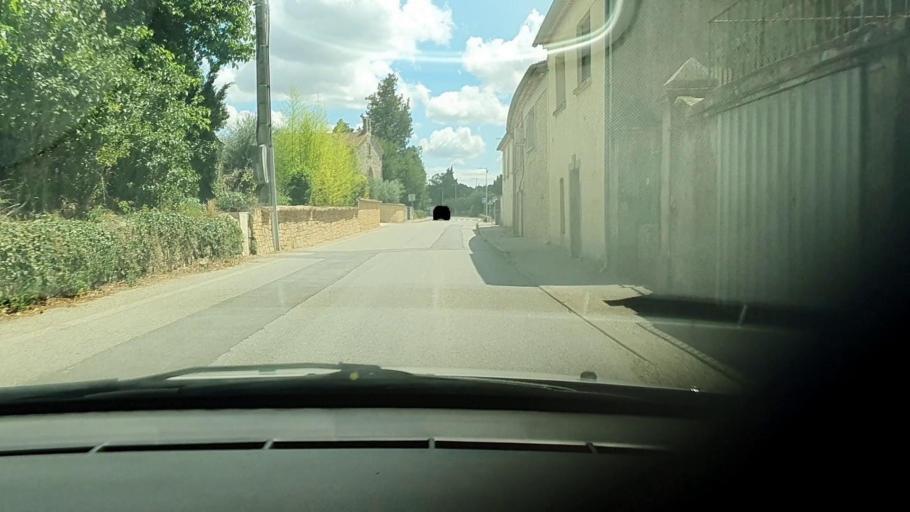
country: FR
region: Languedoc-Roussillon
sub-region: Departement du Gard
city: Moussac
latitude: 44.0510
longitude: 4.2281
